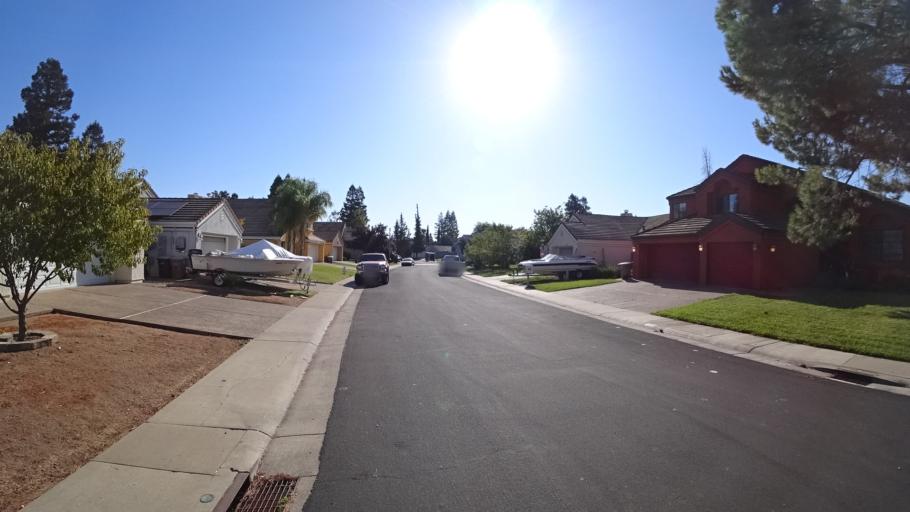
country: US
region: California
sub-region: Sacramento County
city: Laguna
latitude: 38.4293
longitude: -121.4463
